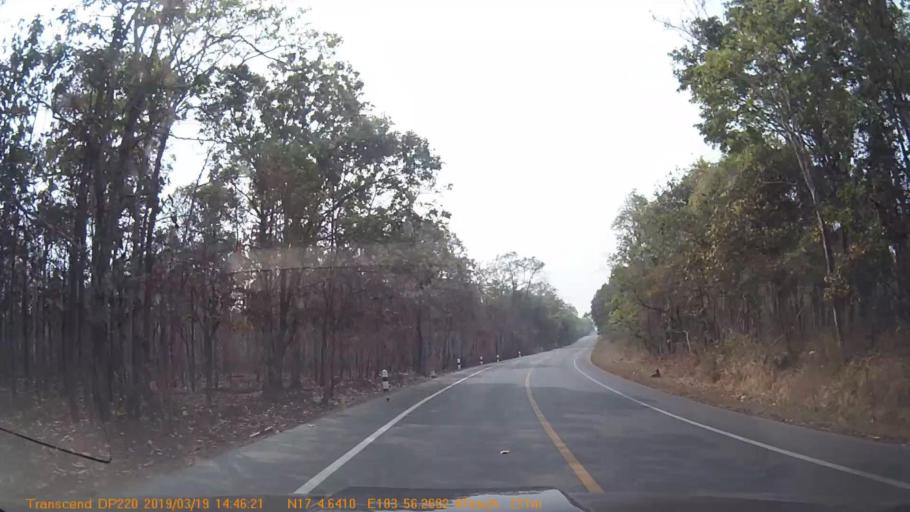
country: TH
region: Sakon Nakhon
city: Phu Phan
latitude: 17.0775
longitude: 103.9375
